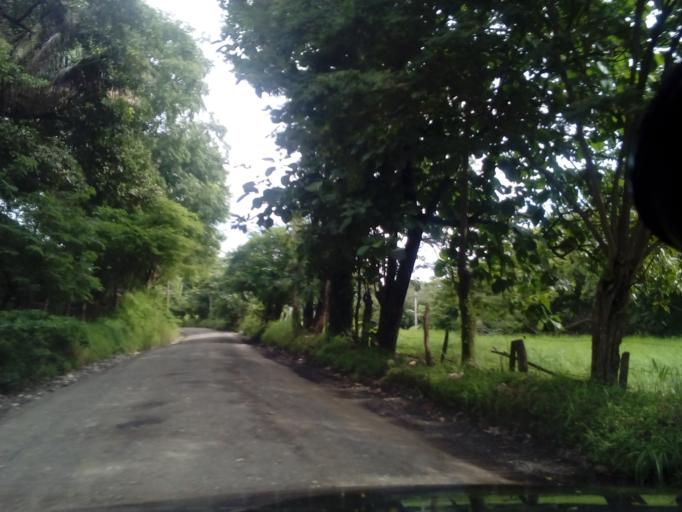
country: CR
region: Guanacaste
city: Samara
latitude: 9.9239
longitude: -85.6576
